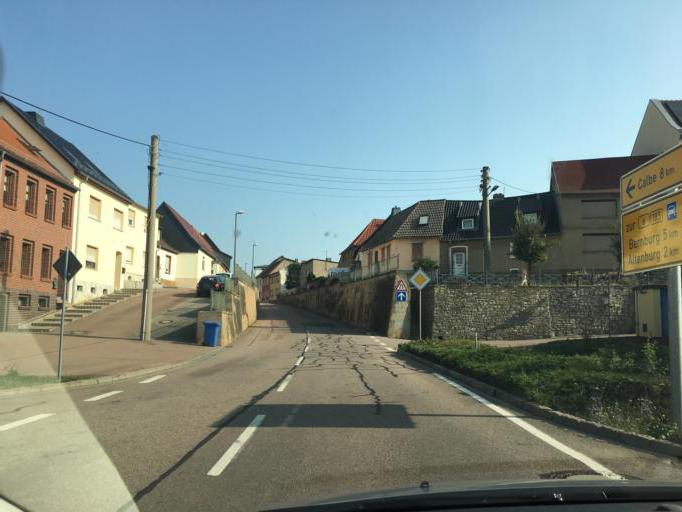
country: DE
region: Saxony-Anhalt
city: Nienburg/Saale
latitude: 51.8339
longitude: 11.7679
